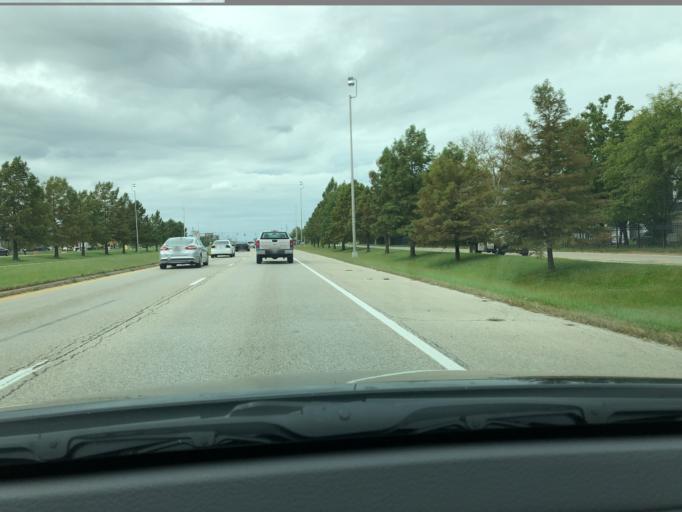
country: US
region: Ohio
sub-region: Franklin County
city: Minerva Park
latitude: 40.0833
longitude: -82.9423
